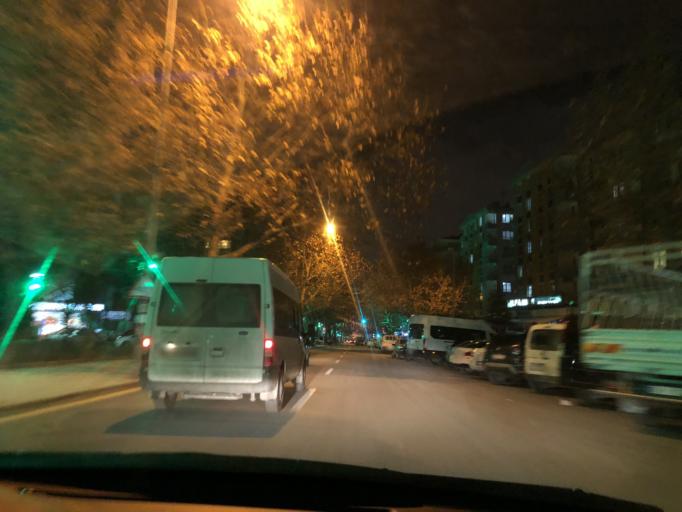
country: TR
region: Ankara
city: Batikent
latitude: 39.9683
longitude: 32.7861
